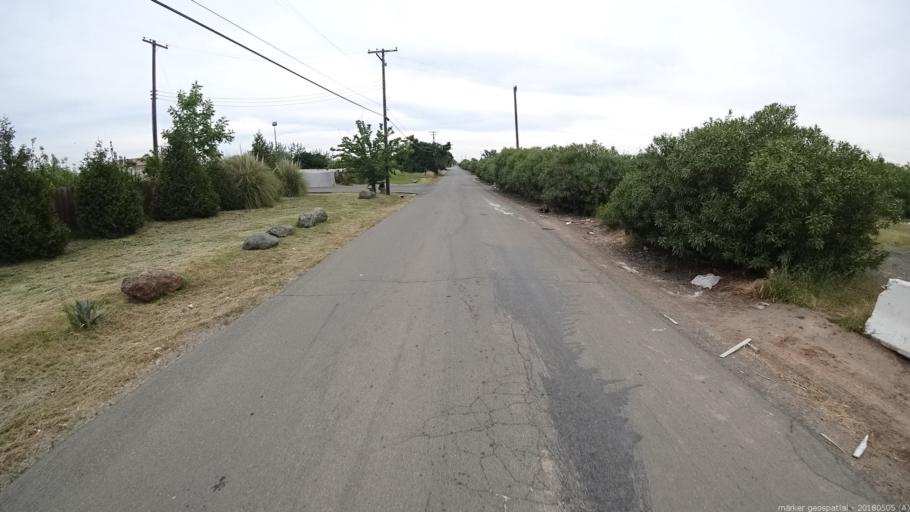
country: US
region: California
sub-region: Sacramento County
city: Rio Linda
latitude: 38.6511
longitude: -121.4353
